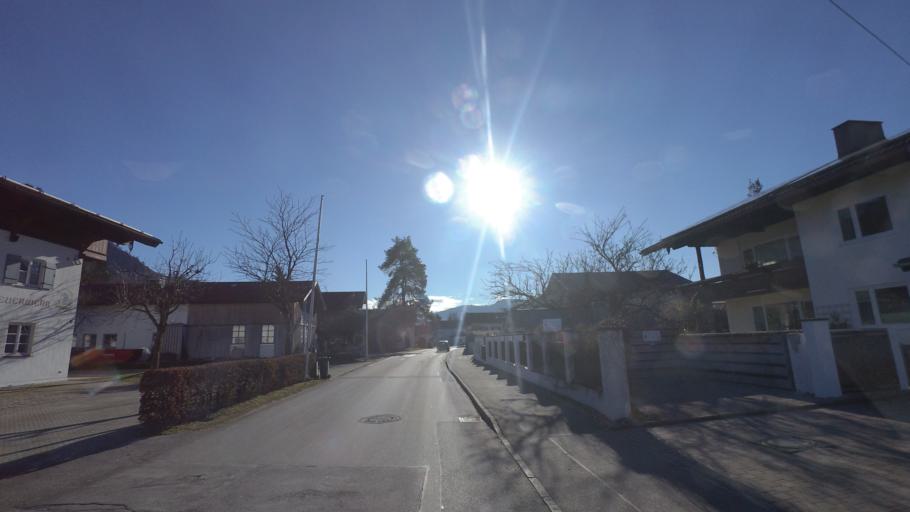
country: DE
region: Bavaria
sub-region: Upper Bavaria
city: Grassau
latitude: 47.7792
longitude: 12.4579
